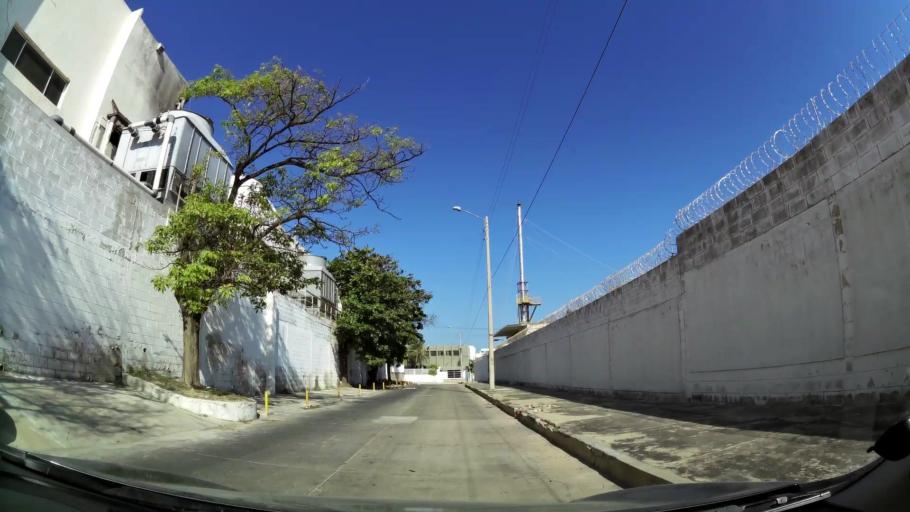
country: CO
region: Atlantico
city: Barranquilla
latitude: 11.0209
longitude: -74.8020
